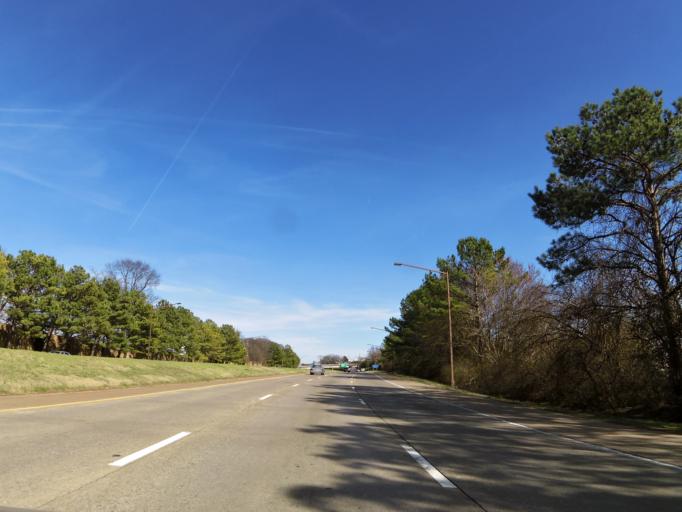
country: US
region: Tennessee
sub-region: Davidson County
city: Oak Hill
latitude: 36.1218
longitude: -86.7610
